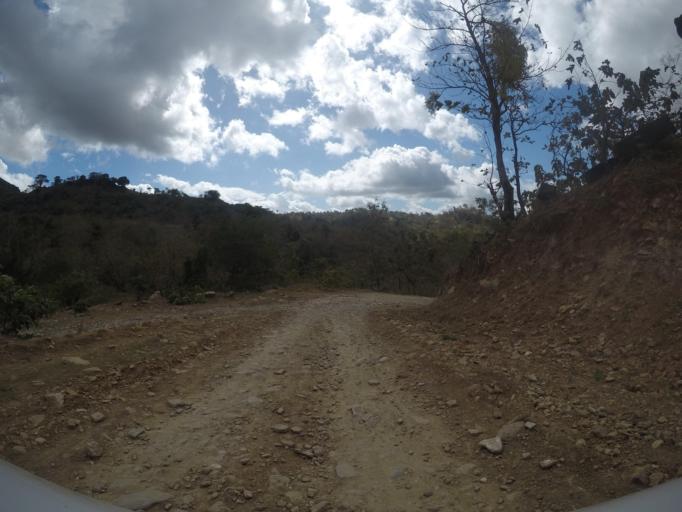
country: TL
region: Lautem
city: Lospalos
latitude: -8.5360
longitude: 126.8361
